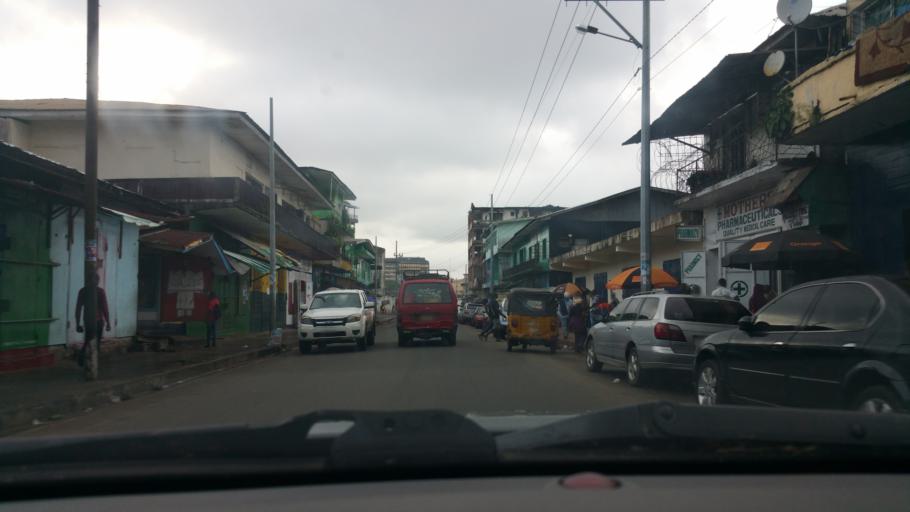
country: LR
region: Montserrado
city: Monrovia
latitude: 6.3082
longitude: -10.7997
